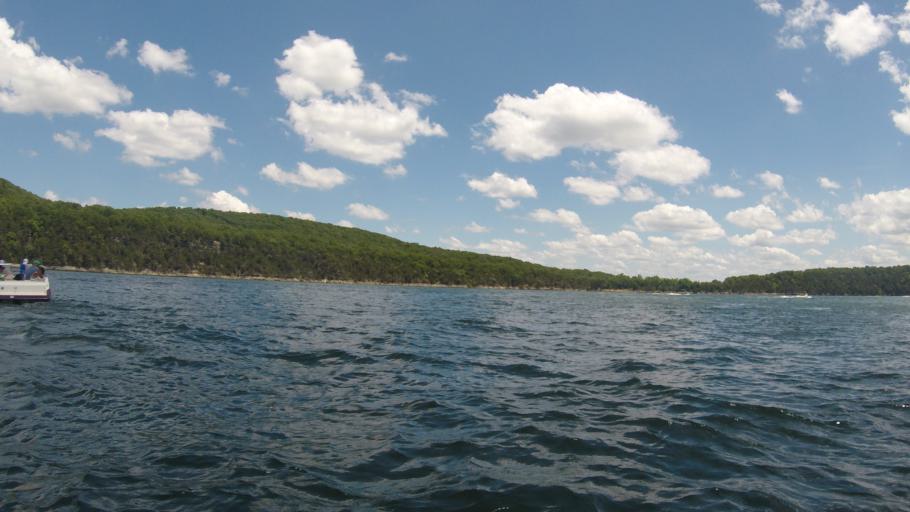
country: US
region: Missouri
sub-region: Barry County
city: Shell Knob
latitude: 36.5970
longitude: -93.5451
